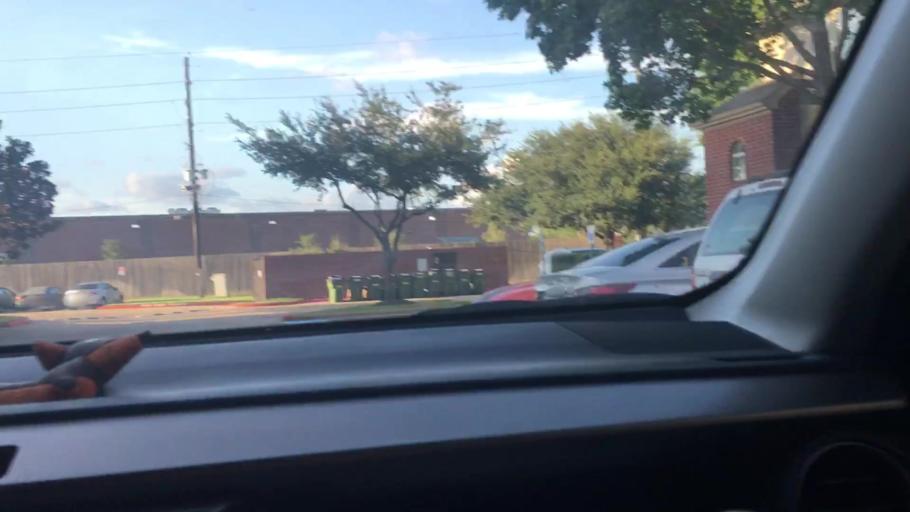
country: US
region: Texas
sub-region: Fort Bend County
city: Meadows Place
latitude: 29.6457
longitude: -95.5828
